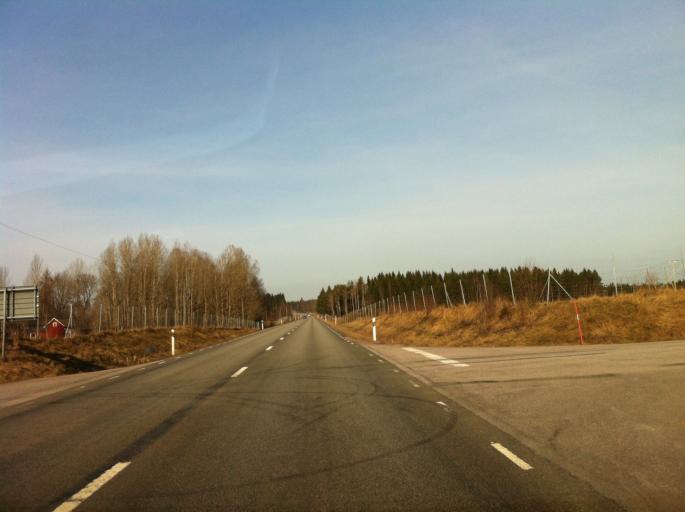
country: SE
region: Vaestra Goetaland
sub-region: Tidaholms Kommun
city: Tidaholm
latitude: 58.1620
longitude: 13.9047
